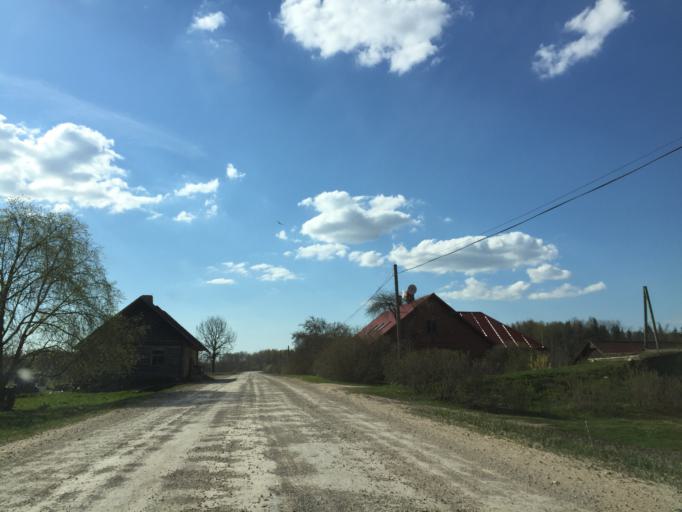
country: LV
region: Krimulda
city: Ragana
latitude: 57.3436
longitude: 24.6036
